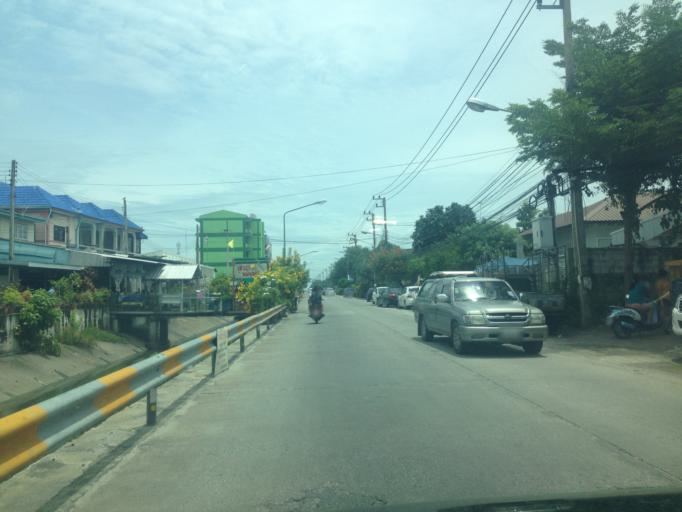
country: TH
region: Chon Buri
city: Chon Buri
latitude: 13.3748
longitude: 100.9866
